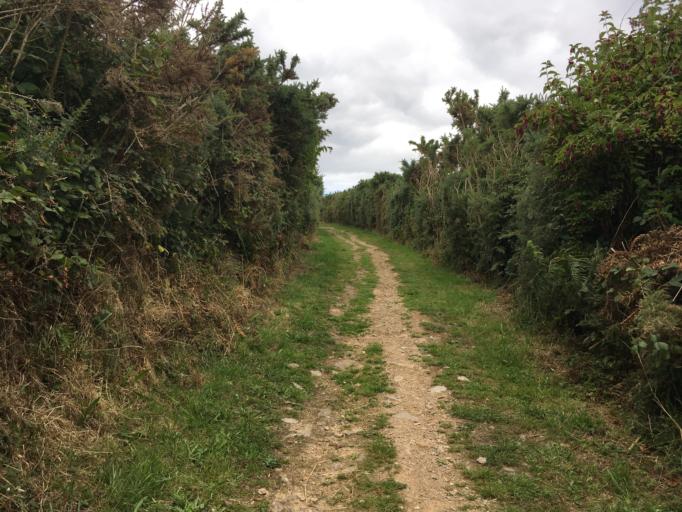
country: IE
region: Munster
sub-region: County Cork
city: Crosshaven
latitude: 51.8064
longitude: -8.2788
